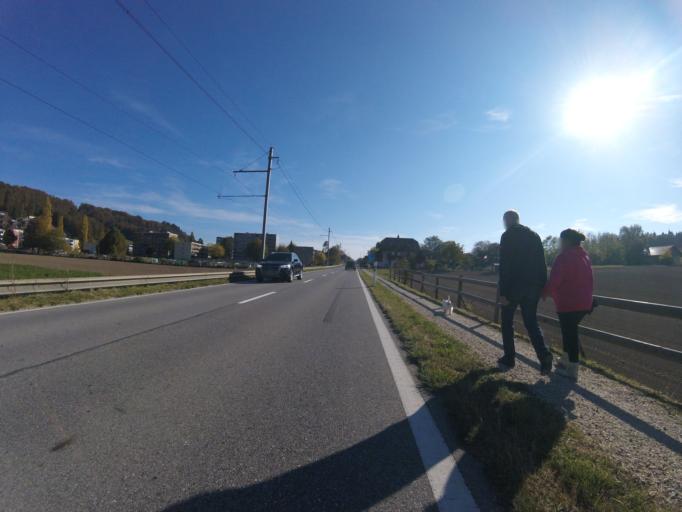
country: CH
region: Bern
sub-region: Bern-Mittelland District
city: Stettlen
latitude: 46.9314
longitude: 7.5232
